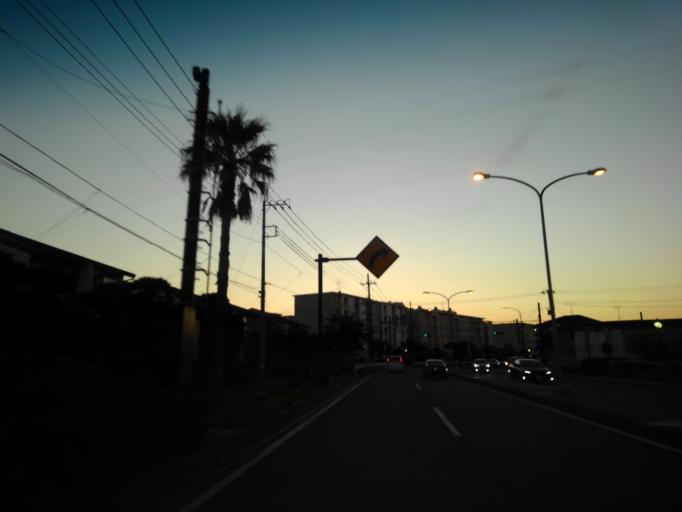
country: JP
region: Kanagawa
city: Yokosuka
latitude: 35.2640
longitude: 139.6984
